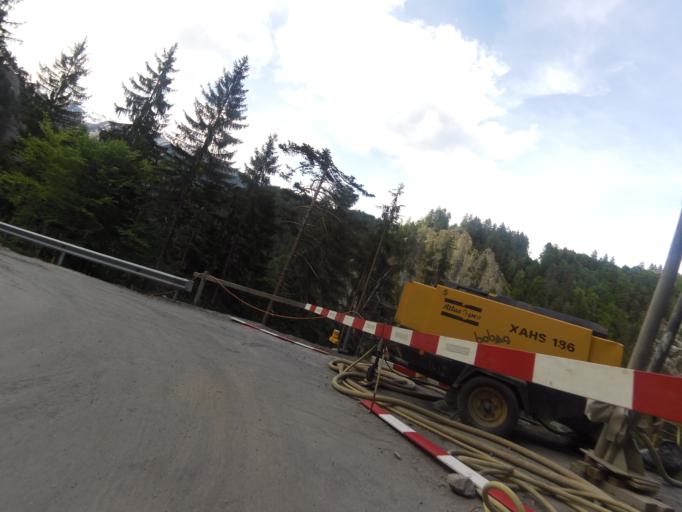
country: CH
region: Grisons
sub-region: Imboden District
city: Rhazuns
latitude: 46.7935
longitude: 9.3406
